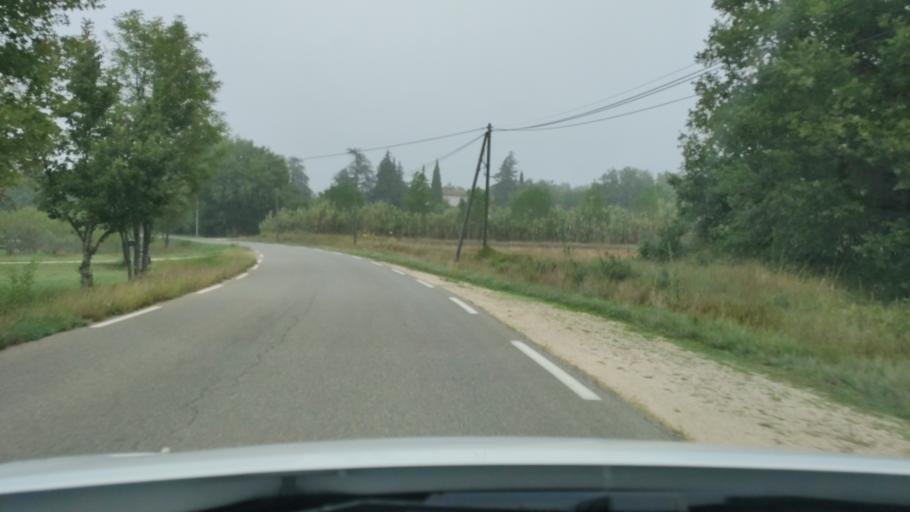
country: FR
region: Provence-Alpes-Cote d'Azur
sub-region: Departement du Vaucluse
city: Bonnieux
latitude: 43.8494
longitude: 5.3117
